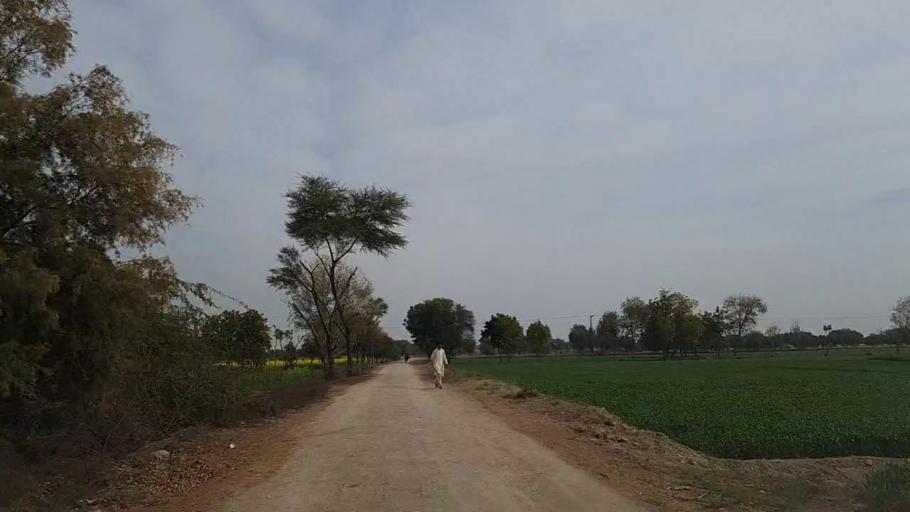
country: PK
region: Sindh
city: Daur
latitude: 26.4106
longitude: 68.4511
